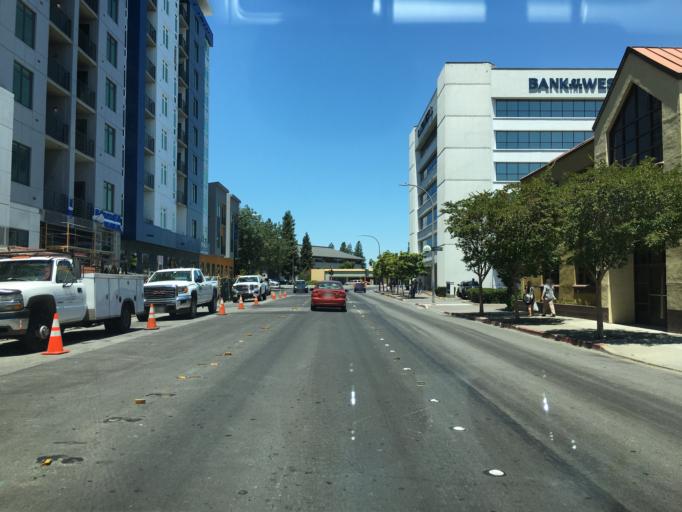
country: US
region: California
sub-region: San Mateo County
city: Redwood City
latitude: 37.4892
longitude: -122.2284
